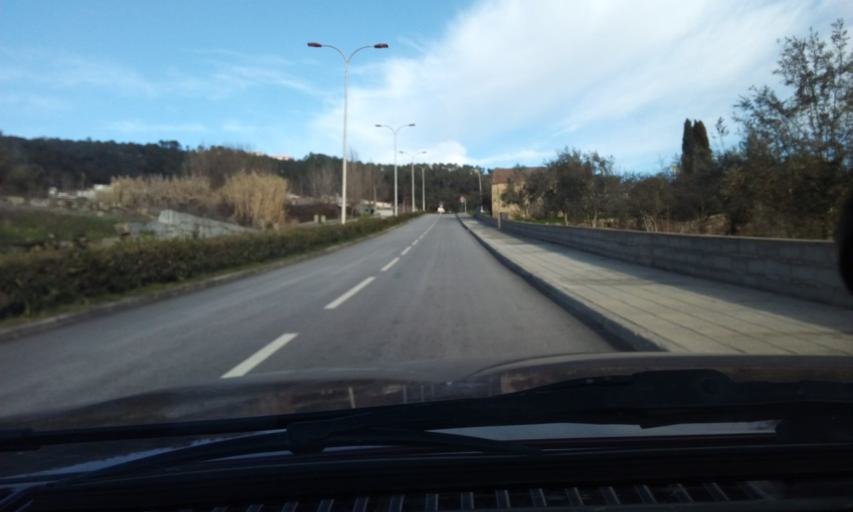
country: PT
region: Guarda
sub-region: Fornos de Algodres
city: Fornos de Algodres
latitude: 40.6179
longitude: -7.5346
